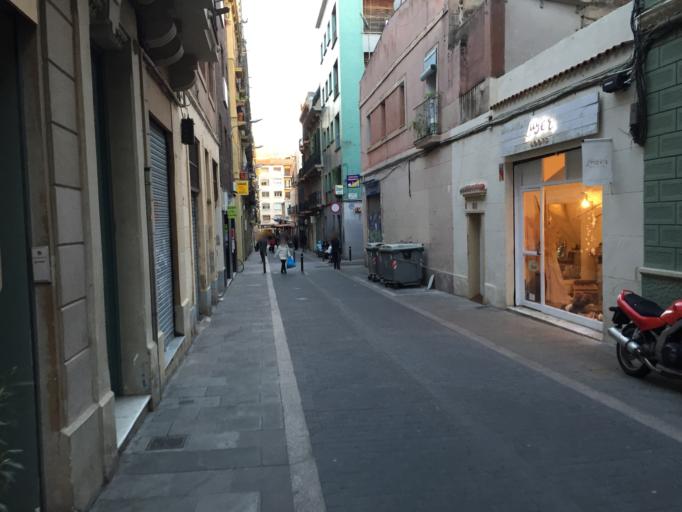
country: ES
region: Catalonia
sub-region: Provincia de Barcelona
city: Gracia
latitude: 41.4033
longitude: 2.1590
